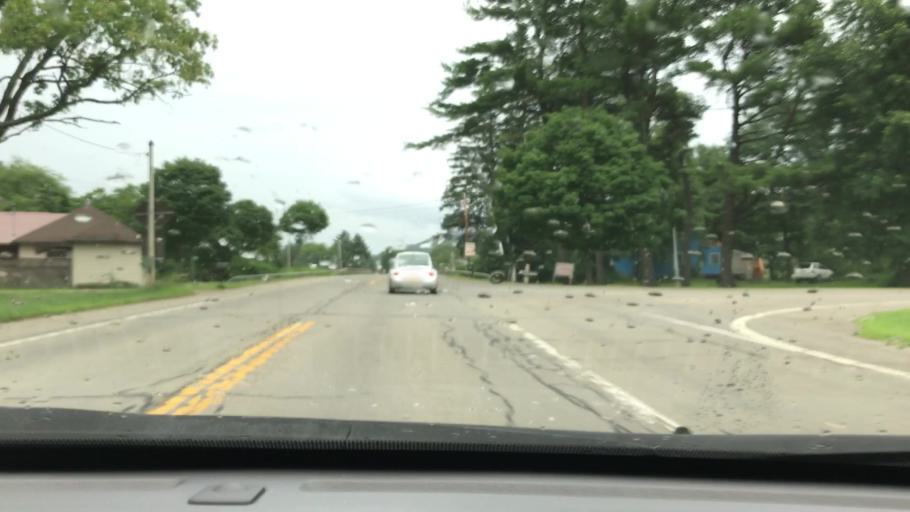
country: US
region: New York
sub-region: Cattaraugus County
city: Salamanca
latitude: 42.1936
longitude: -78.6658
